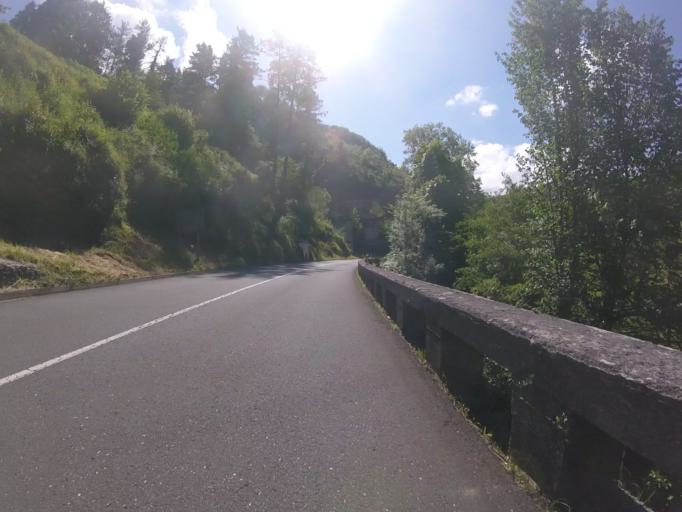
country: ES
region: Basque Country
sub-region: Provincia de Guipuzcoa
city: Azpeitia
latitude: 43.1783
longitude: -2.2246
